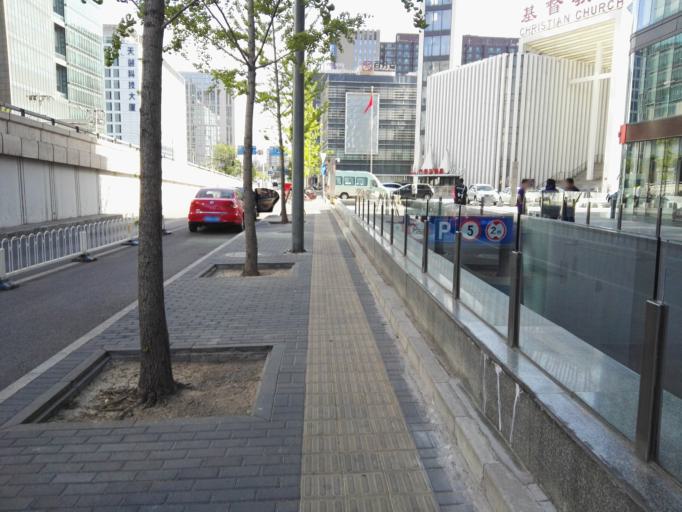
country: CN
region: Beijing
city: Haidian
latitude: 39.9826
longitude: 116.3019
